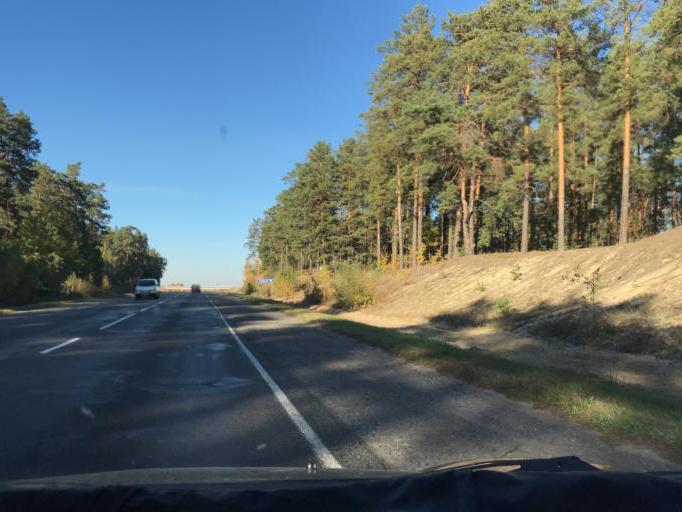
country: BY
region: Gomel
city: Kalinkavichy
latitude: 52.0678
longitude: 29.3610
